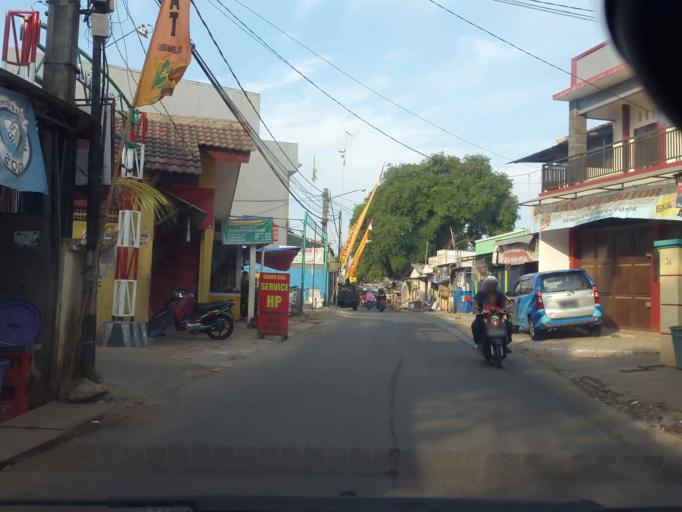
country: ID
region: West Java
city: Ciputat
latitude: -6.2452
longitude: 106.6899
